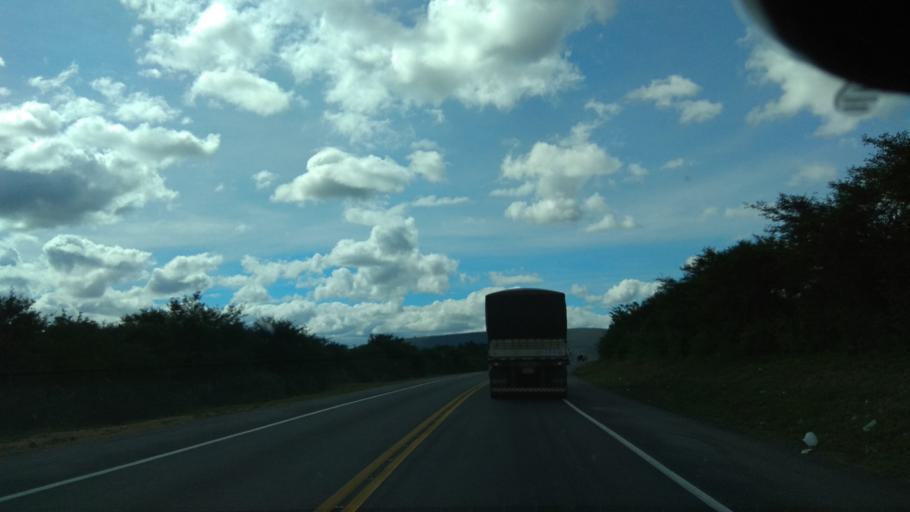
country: BR
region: Bahia
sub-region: Santa Ines
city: Santa Ines
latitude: -13.2894
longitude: -40.0223
